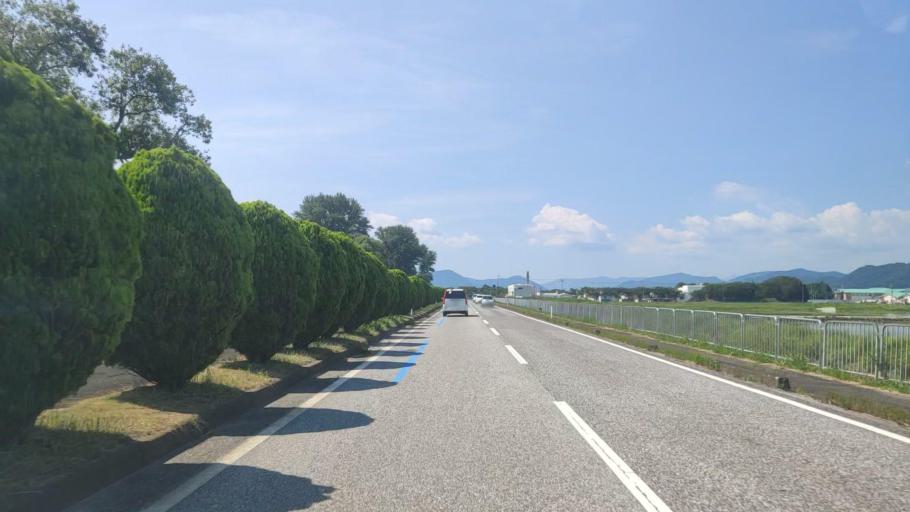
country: JP
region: Shiga Prefecture
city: Nagahama
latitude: 35.4220
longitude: 136.1988
